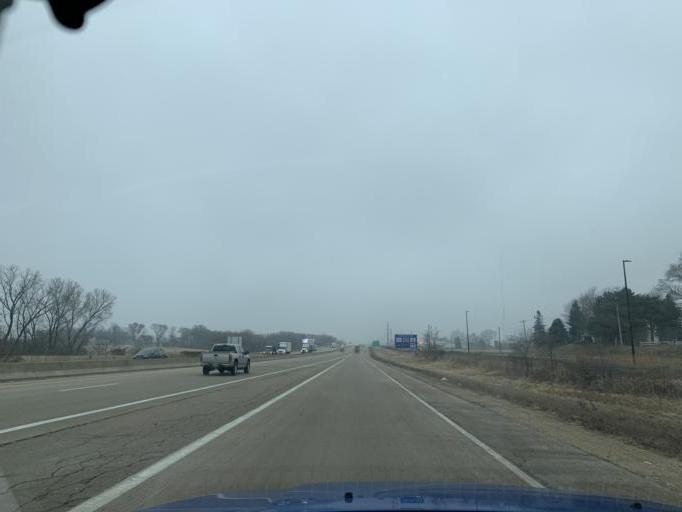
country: US
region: Wisconsin
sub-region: Dane County
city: Sun Prairie
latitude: 43.1728
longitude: -89.2538
